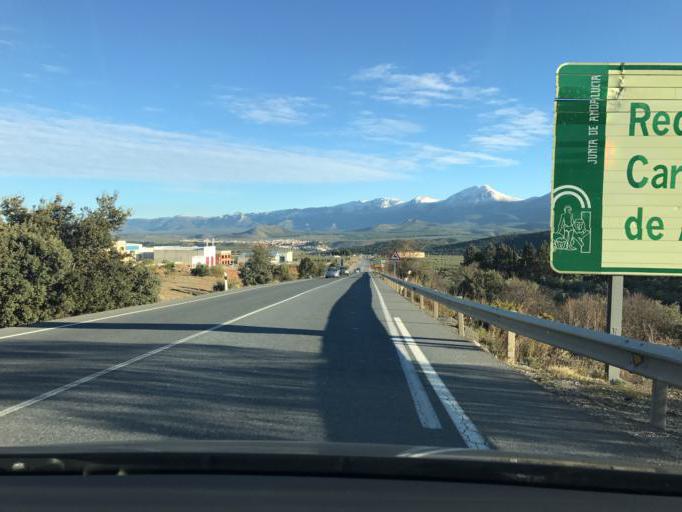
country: ES
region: Andalusia
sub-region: Provincia de Granada
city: Iznalloz
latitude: 37.4052
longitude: -3.5632
